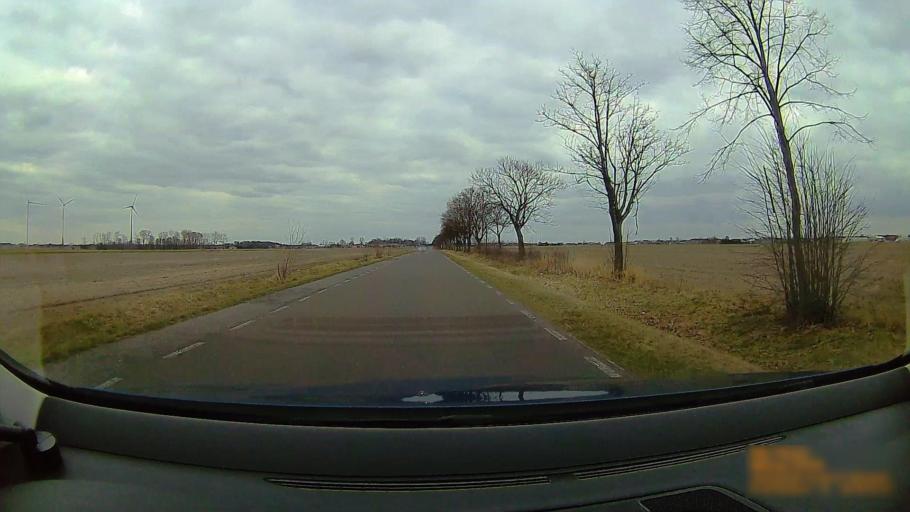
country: PL
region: Greater Poland Voivodeship
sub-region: Powiat koninski
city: Rychwal
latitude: 52.0973
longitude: 18.1231
